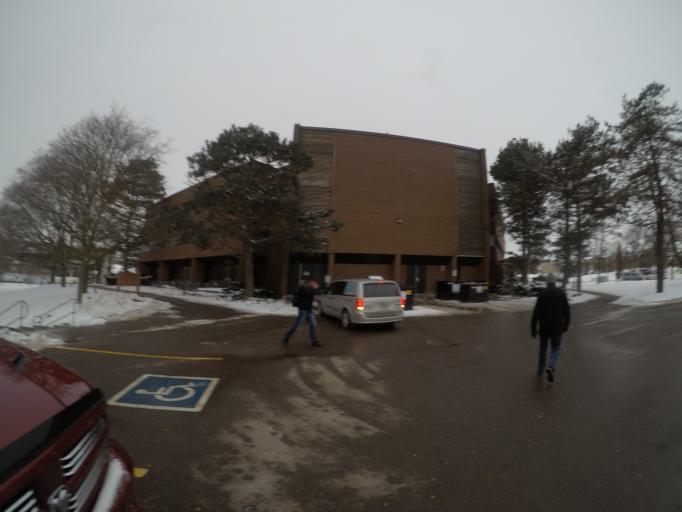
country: CA
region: Ontario
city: Waterloo
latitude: 43.4739
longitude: -80.5447
